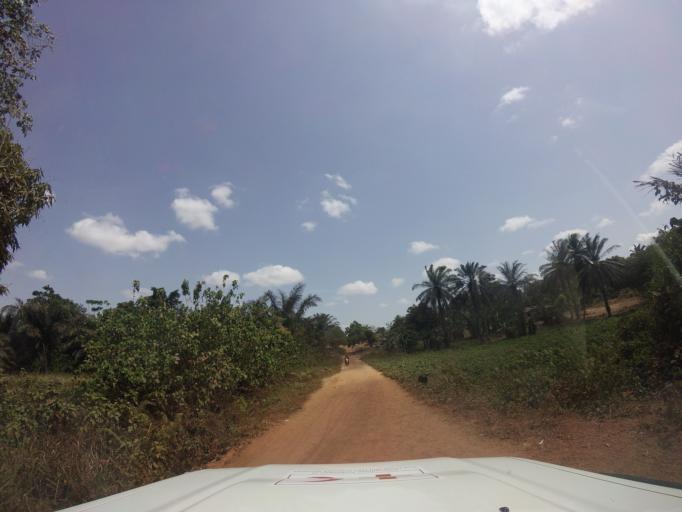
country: SL
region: Southern Province
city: Zimmi
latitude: 7.0434
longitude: -11.2820
